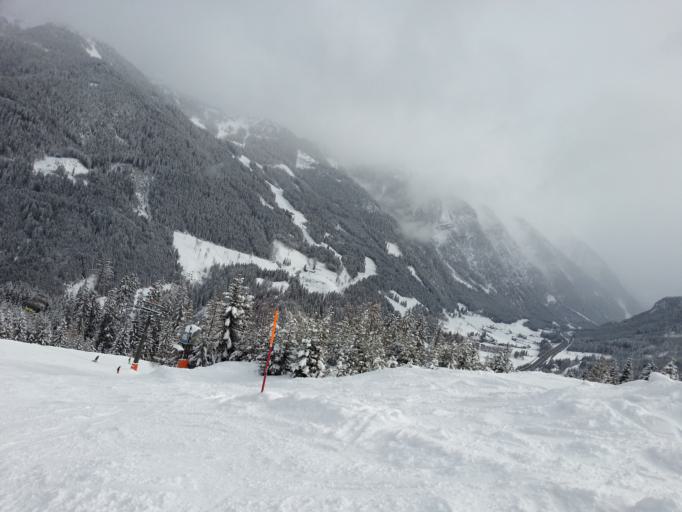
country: AT
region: Salzburg
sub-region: Politischer Bezirk Sankt Johann im Pongau
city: Flachau
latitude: 47.3050
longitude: 13.3808
